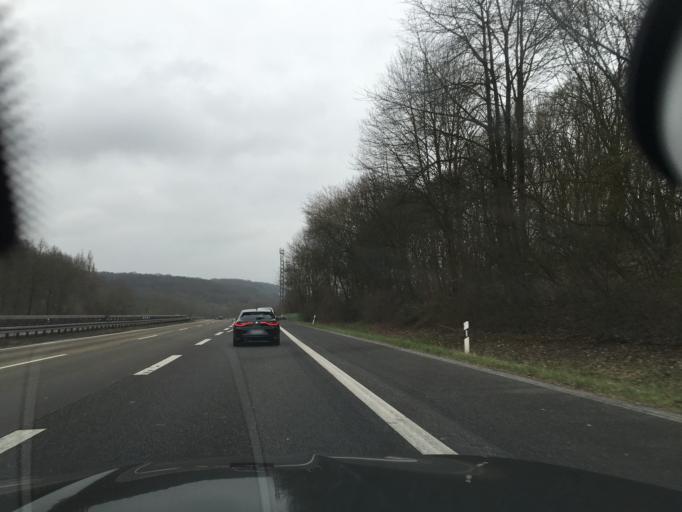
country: DE
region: North Rhine-Westphalia
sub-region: Regierungsbezirk Koln
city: Konigswinter
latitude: 50.7293
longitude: 7.1555
